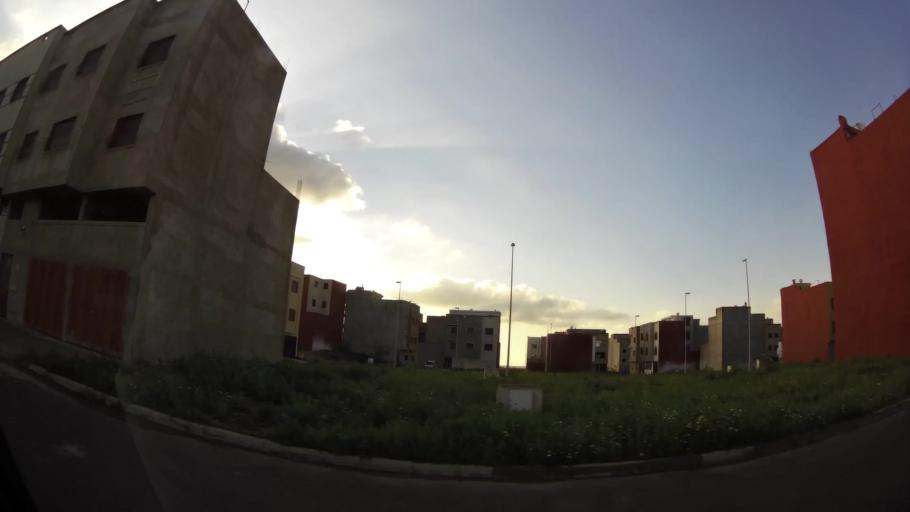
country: MA
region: Chaouia-Ouardigha
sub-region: Settat Province
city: Settat
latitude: 32.9865
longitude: -7.6372
